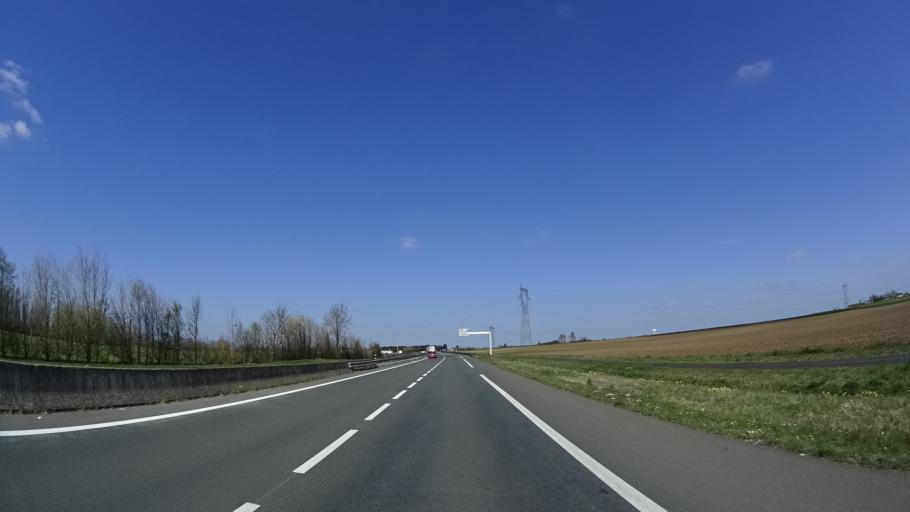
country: FR
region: Pays de la Loire
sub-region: Departement de Maine-et-Loire
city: Doue-la-Fontaine
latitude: 47.2266
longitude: -0.3081
